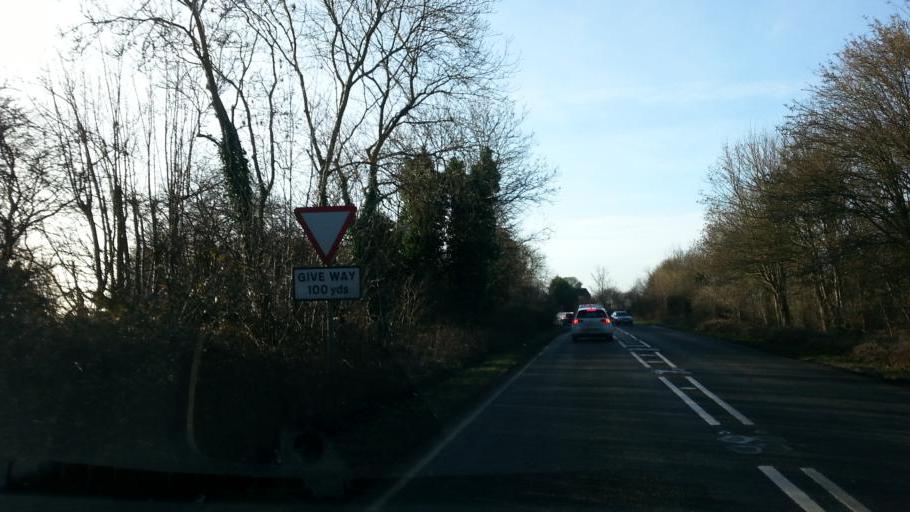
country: GB
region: England
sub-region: Lincolnshire
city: Grantham
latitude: 52.9037
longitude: -0.5871
